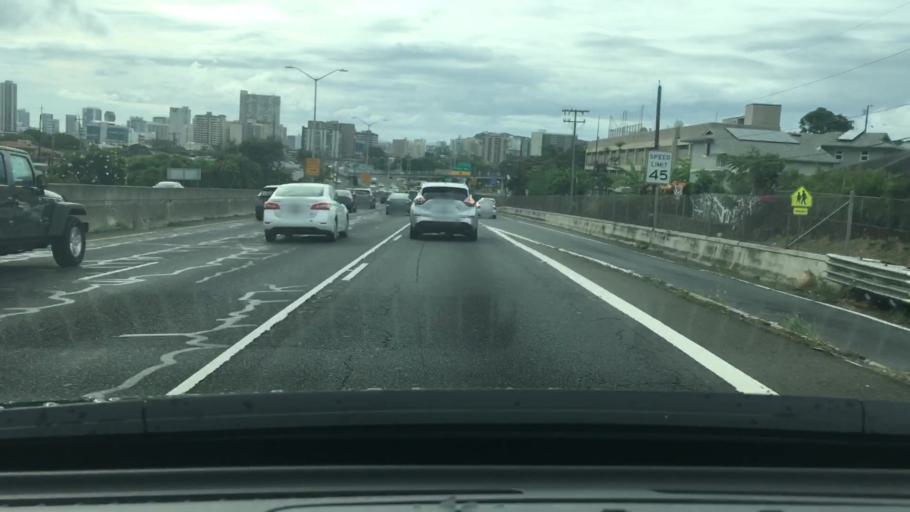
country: US
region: Hawaii
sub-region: Honolulu County
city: Honolulu
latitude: 21.2952
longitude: -157.8220
